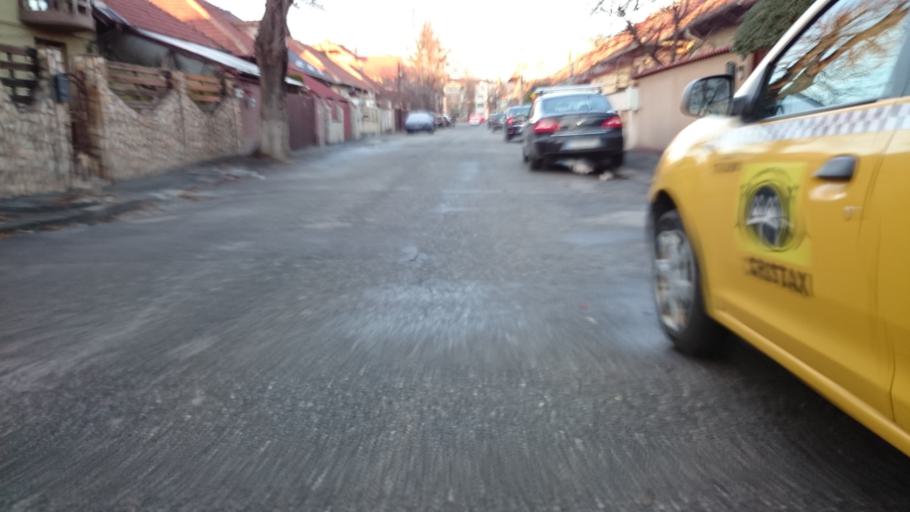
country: RO
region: Bucuresti
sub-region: Municipiul Bucuresti
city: Bucuresti
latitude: 44.4248
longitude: 26.0586
